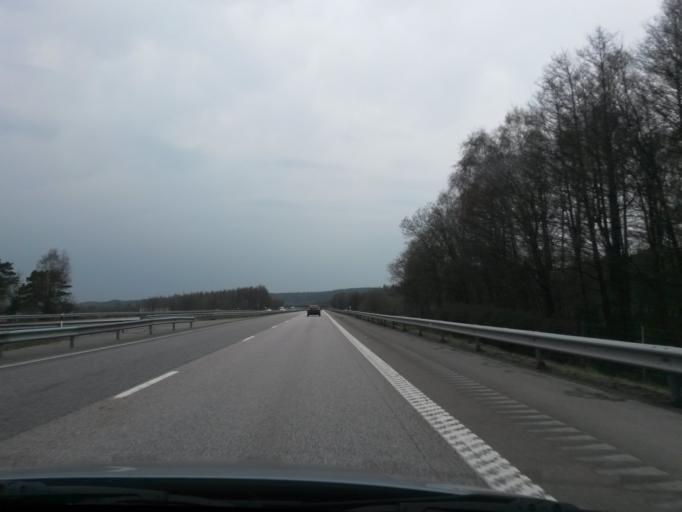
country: SE
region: Halland
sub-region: Varbergs Kommun
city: Veddige
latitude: 57.2148
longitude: 12.2393
